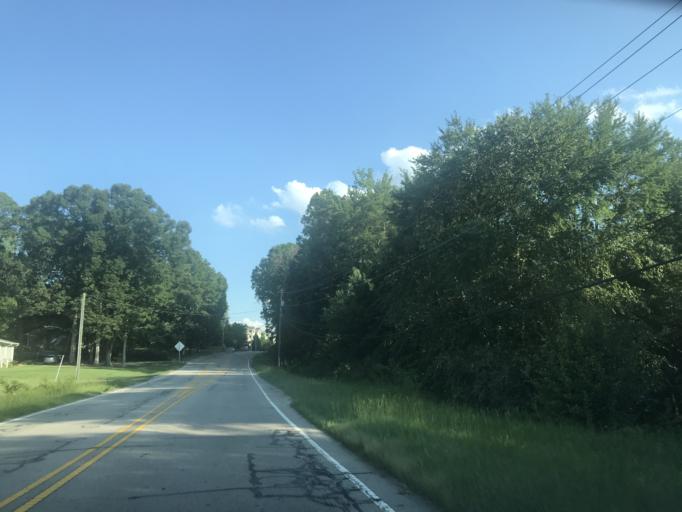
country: US
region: North Carolina
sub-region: Wake County
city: Knightdale
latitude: 35.7772
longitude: -78.5252
